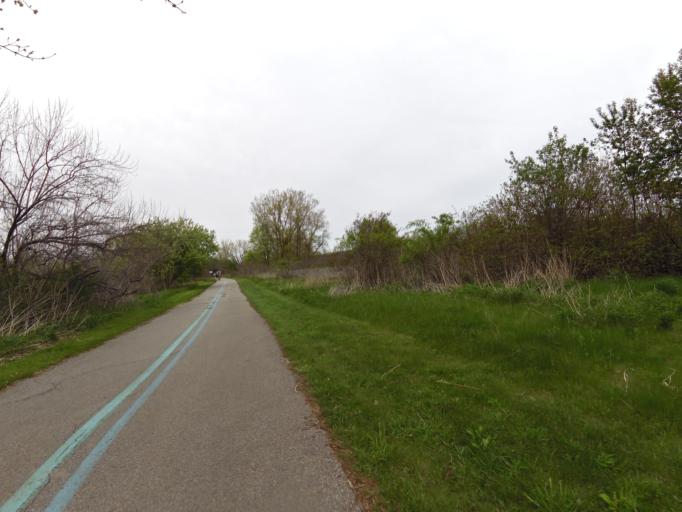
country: CA
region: Ontario
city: Toronto
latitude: 43.6460
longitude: -79.3321
